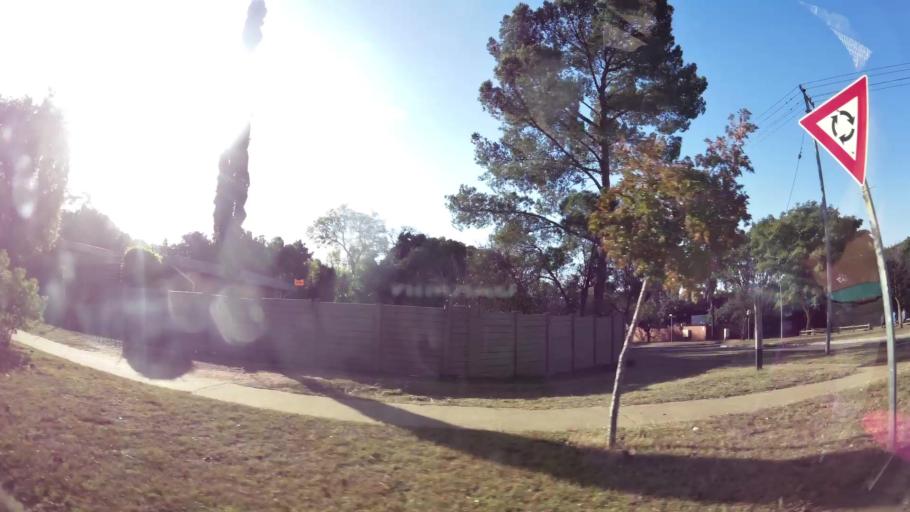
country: ZA
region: Gauteng
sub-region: City of Tshwane Metropolitan Municipality
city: Pretoria
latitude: -25.7298
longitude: 28.2135
